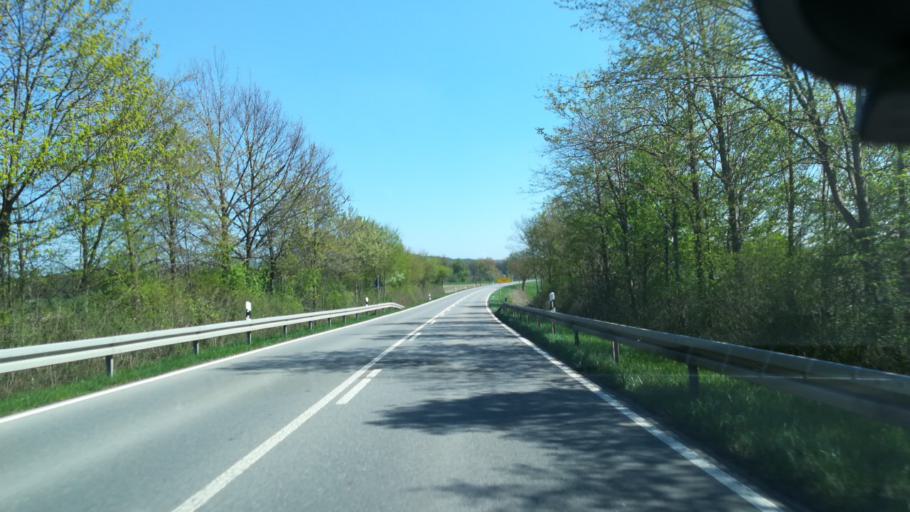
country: DE
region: Baden-Wuerttemberg
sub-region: Freiburg Region
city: Muhlhausen-Ehingen
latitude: 47.7978
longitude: 8.8407
